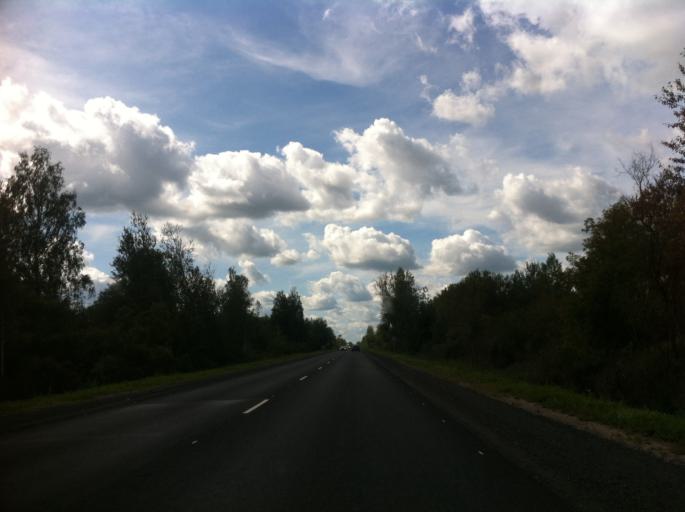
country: RU
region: Pskov
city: Izborsk
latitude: 57.7479
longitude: 28.0395
